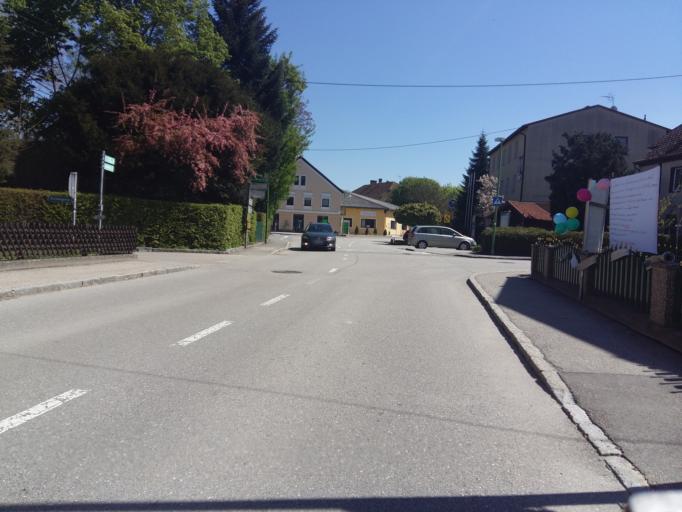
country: AT
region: Upper Austria
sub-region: Politischer Bezirk Scharding
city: Sankt Marienkirchen bei Schaerding
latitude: 48.3878
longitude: 13.4500
